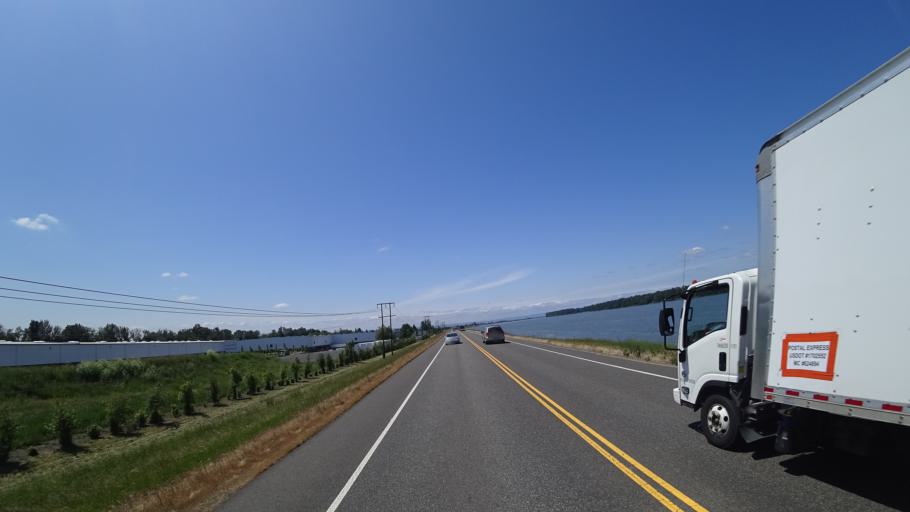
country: US
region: Oregon
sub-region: Multnomah County
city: Fairview
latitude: 45.5598
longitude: -122.4858
